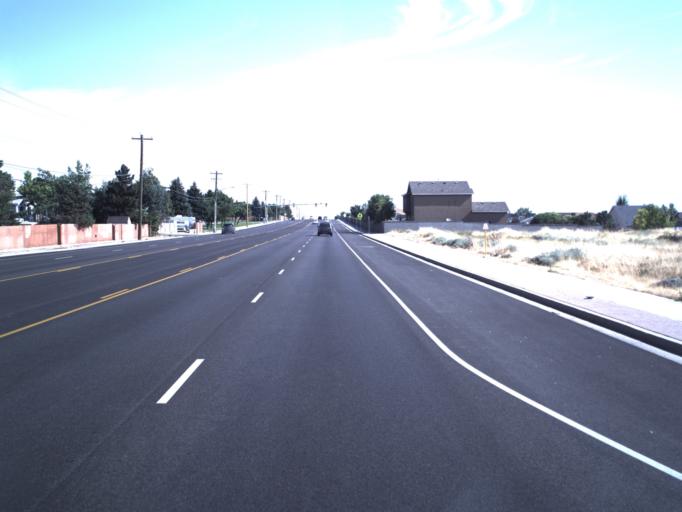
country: US
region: Utah
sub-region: Salt Lake County
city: Oquirrh
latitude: 40.6424
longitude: -112.0245
